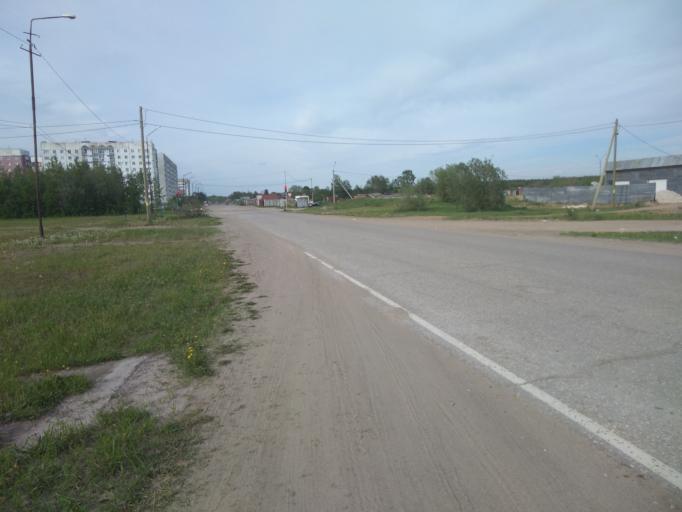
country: RU
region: Komi Republic
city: Pechora
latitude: 65.1443
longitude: 57.2363
